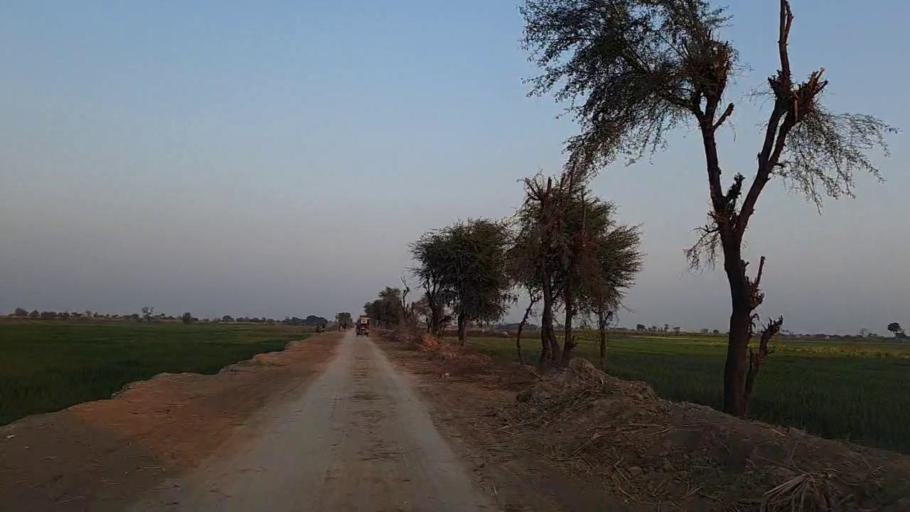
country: PK
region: Sindh
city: Jam Sahib
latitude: 26.3050
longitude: 68.5666
